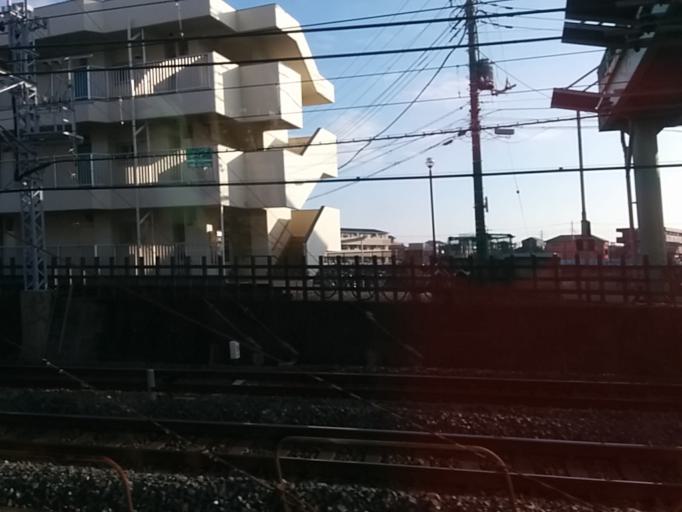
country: JP
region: Saitama
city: Asaka
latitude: 35.8043
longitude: 139.5979
